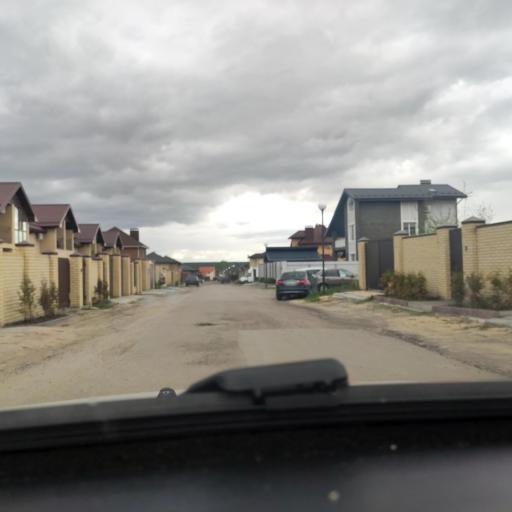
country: RU
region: Voronezj
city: Podgornoye
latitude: 51.7552
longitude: 39.1471
